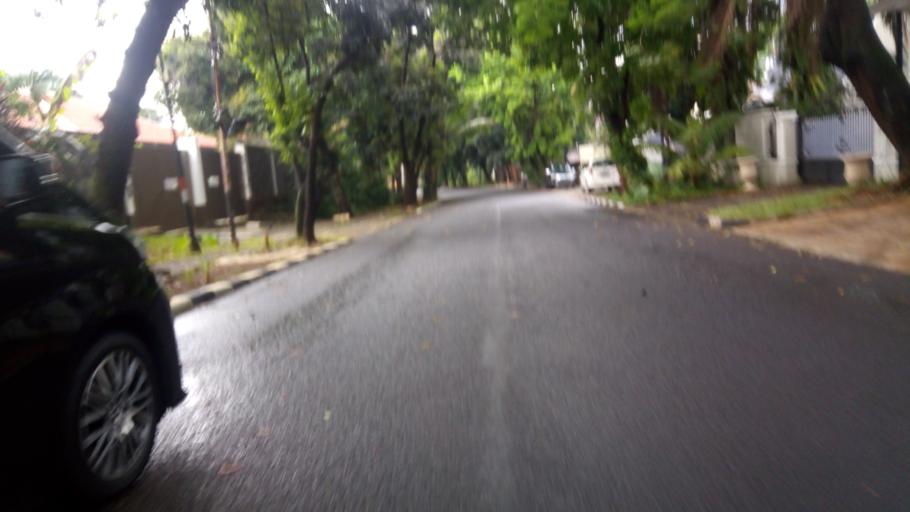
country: ID
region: Jakarta Raya
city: Jakarta
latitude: -6.2561
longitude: 106.8066
